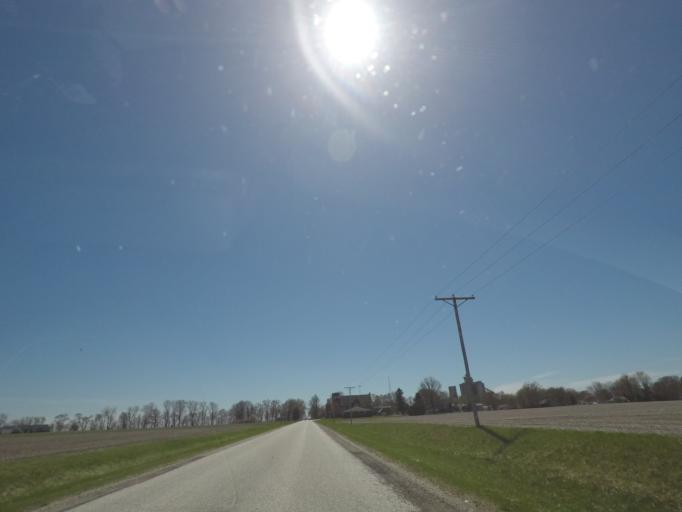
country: US
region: Illinois
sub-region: Logan County
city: Mount Pulaski
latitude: 40.0579
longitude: -89.1825
